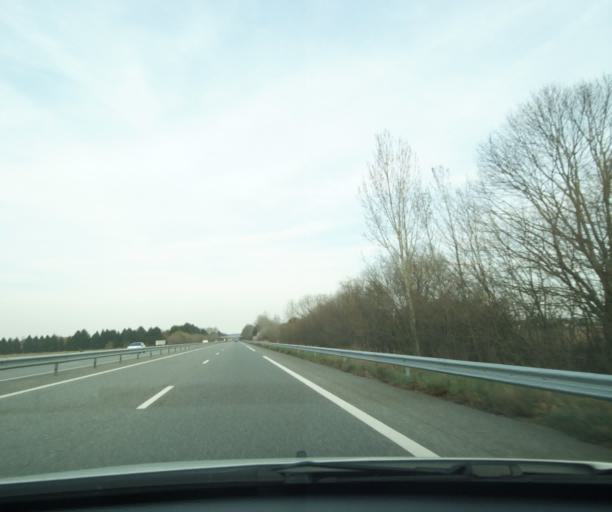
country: FR
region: Midi-Pyrenees
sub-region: Departement des Hautes-Pyrenees
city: Laloubere
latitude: 43.2102
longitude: 0.0604
